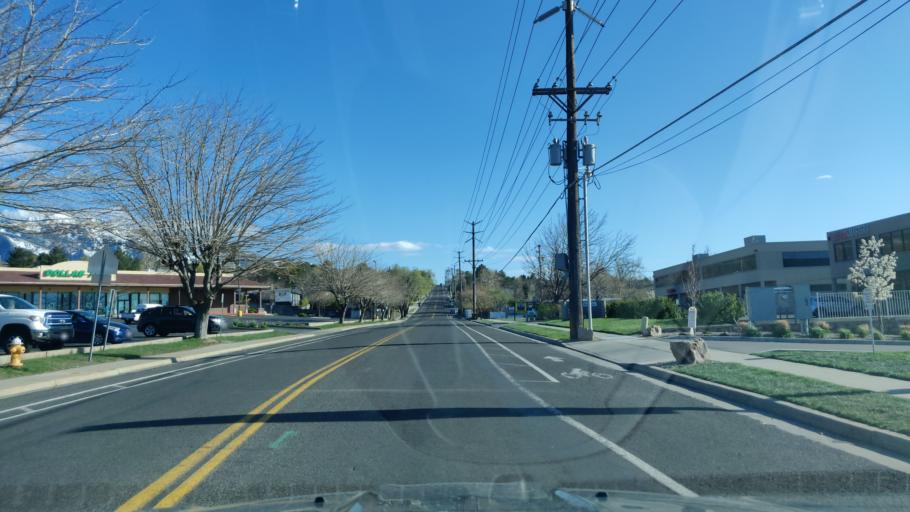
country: US
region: Utah
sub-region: Salt Lake County
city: Cottonwood Heights
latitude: 40.6231
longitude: -111.8248
